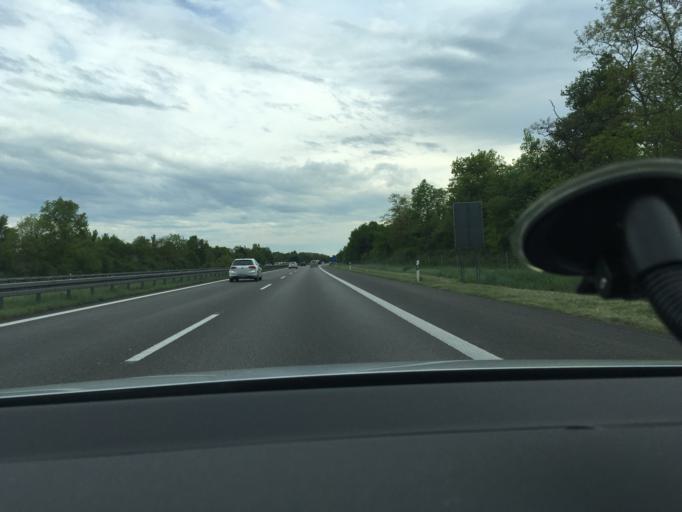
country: DE
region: Baden-Wuerttemberg
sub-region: Freiburg Region
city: Neuenburg am Rhein
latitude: 47.8355
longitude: 7.5650
